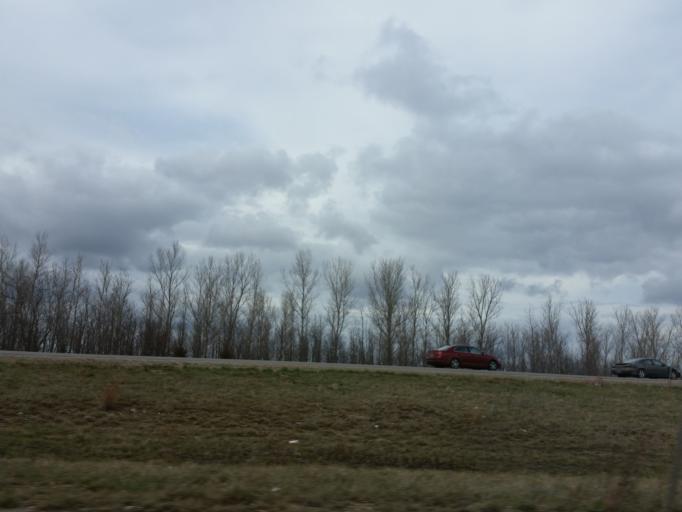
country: US
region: Iowa
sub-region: Black Hawk County
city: Elk Run Heights
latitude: 42.4490
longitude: -92.1969
